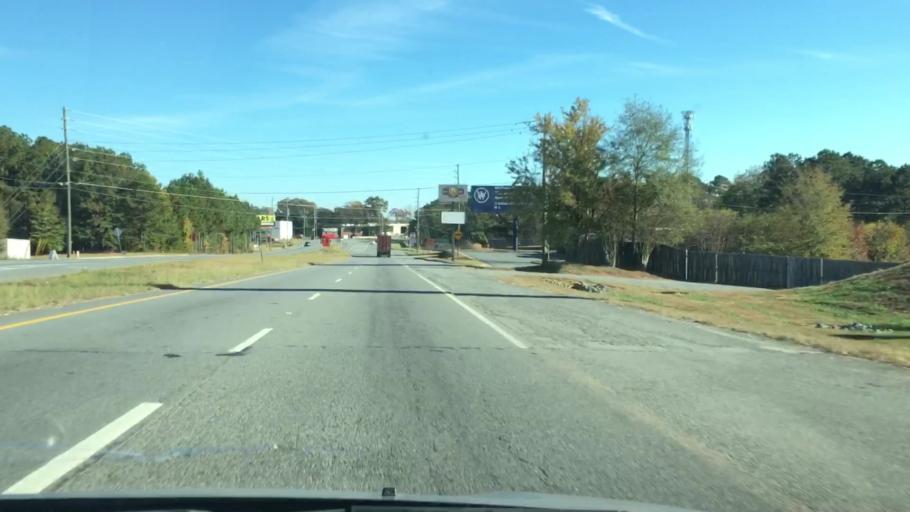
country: US
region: Georgia
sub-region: Fulton County
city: Milton
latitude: 34.1300
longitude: -84.2294
